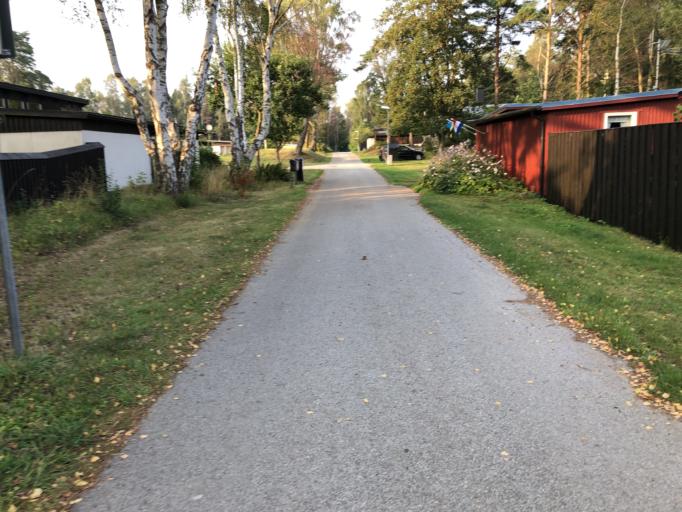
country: SE
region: Skane
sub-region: Ystads Kommun
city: Kopingebro
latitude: 55.4302
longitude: 13.9504
